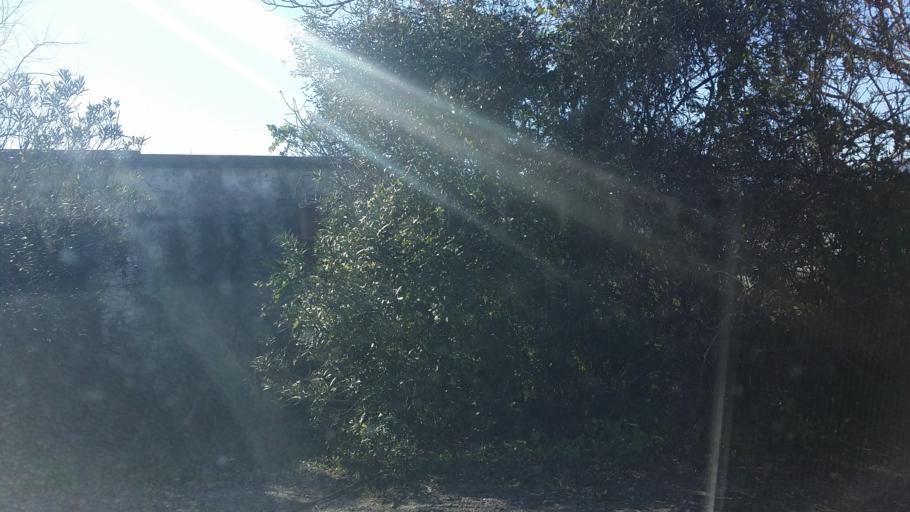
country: GR
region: West Greece
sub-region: Nomos Aitolias kai Akarnanias
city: Fitiai
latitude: 38.7072
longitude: 21.1712
